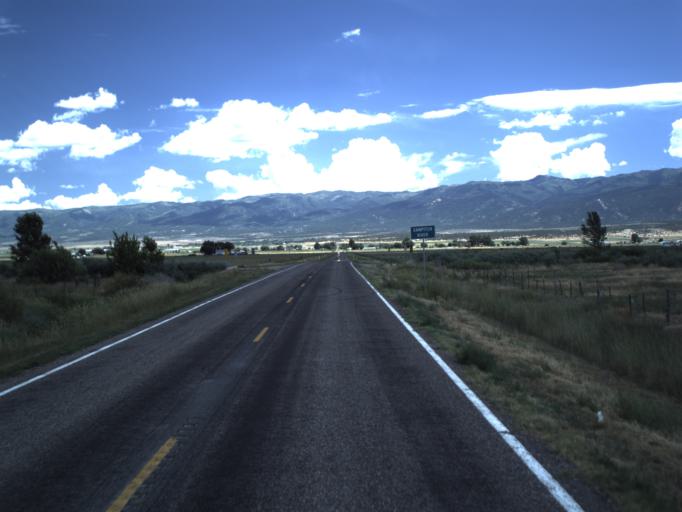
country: US
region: Utah
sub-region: Sanpete County
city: Moroni
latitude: 39.4757
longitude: -111.5979
